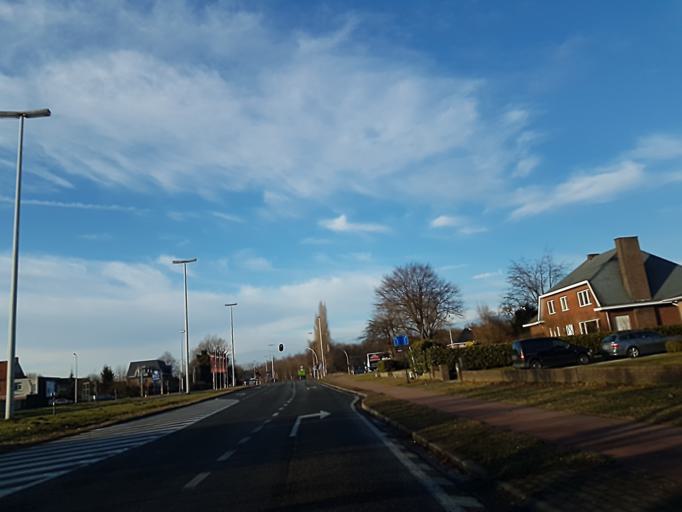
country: BE
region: Flanders
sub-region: Provincie Antwerpen
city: Turnhout
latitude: 51.3324
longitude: 4.9618
